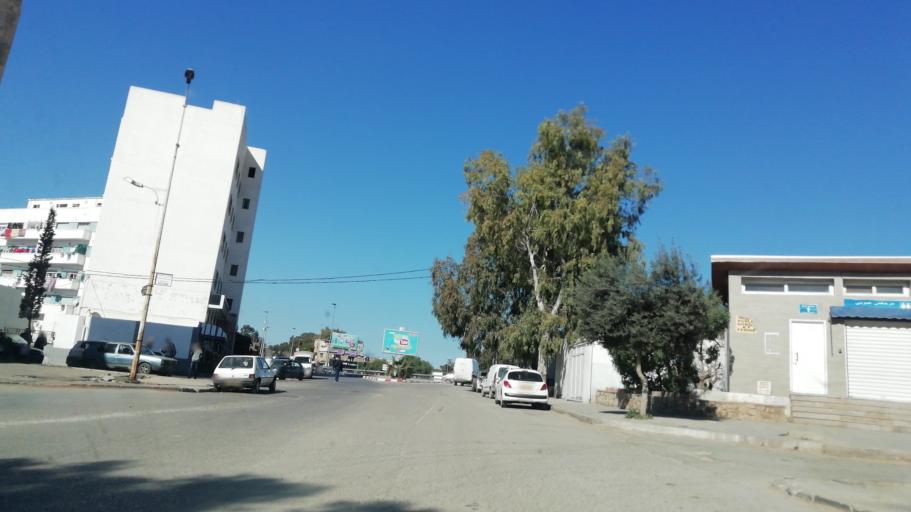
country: DZ
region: Oran
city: Oran
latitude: 35.6962
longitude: -0.6123
